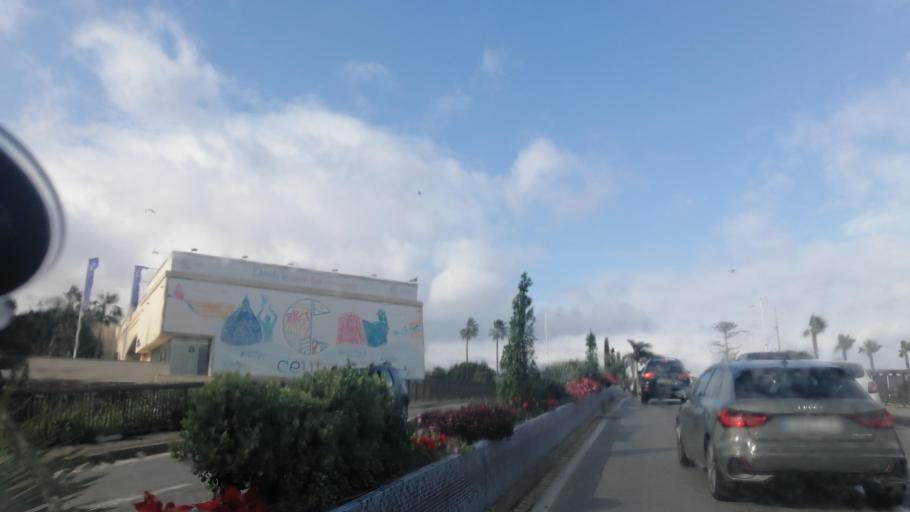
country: ES
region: Ceuta
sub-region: Ceuta
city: Ceuta
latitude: 35.8895
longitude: -5.3171
